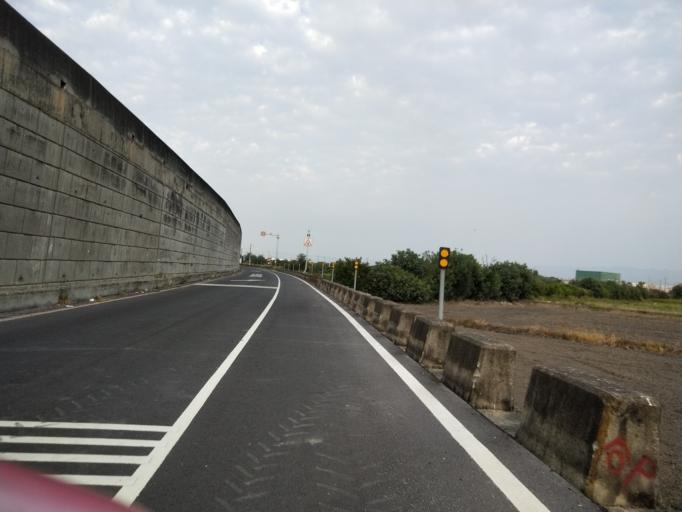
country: TW
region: Taiwan
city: Fengyuan
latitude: 24.3906
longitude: 120.6010
